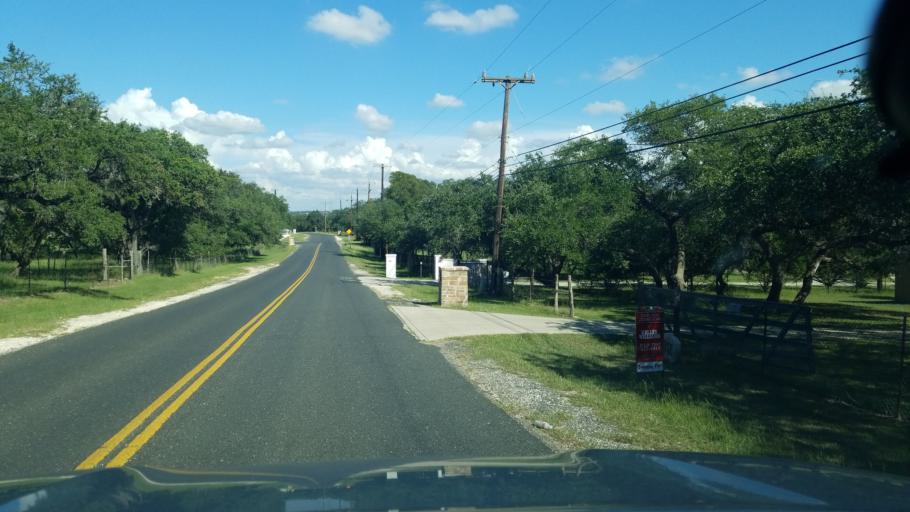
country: US
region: Texas
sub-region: Bexar County
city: Timberwood Park
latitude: 29.6765
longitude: -98.4984
